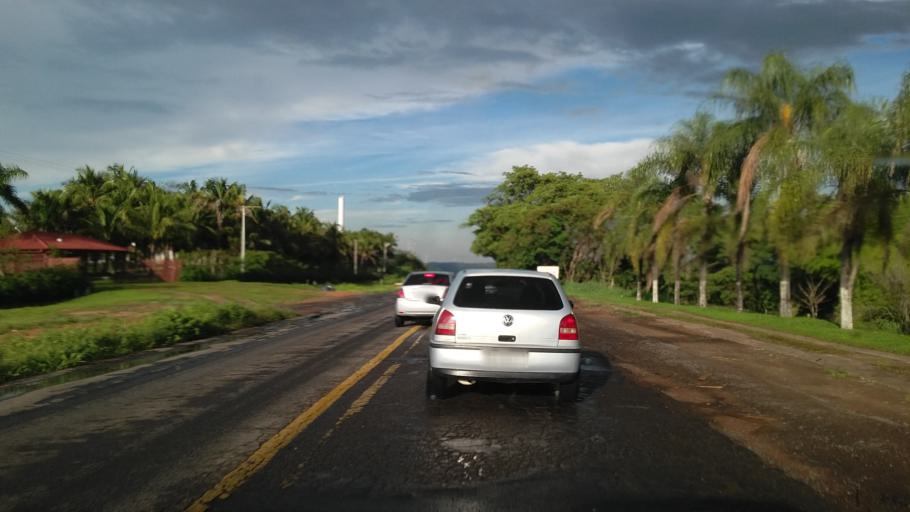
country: BR
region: Sao Paulo
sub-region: Marilia
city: Marilia
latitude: -22.1294
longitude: -49.9395
